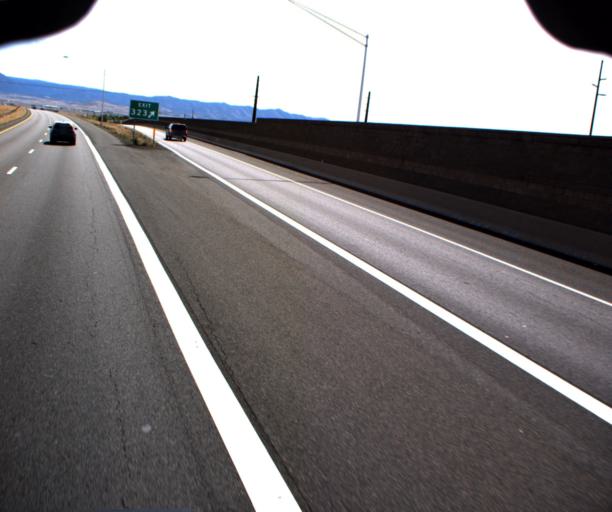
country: US
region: Arizona
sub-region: Yavapai County
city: Prescott Valley
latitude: 34.6351
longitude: -112.3387
